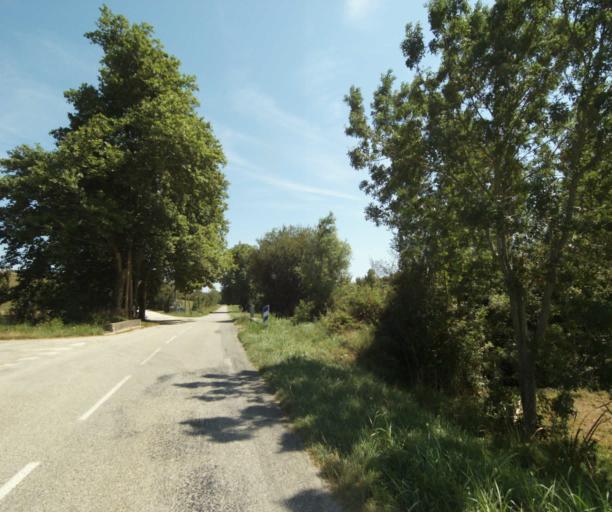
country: FR
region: Midi-Pyrenees
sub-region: Departement de l'Ariege
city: Lezat-sur-Leze
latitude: 43.2269
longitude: 1.3943
